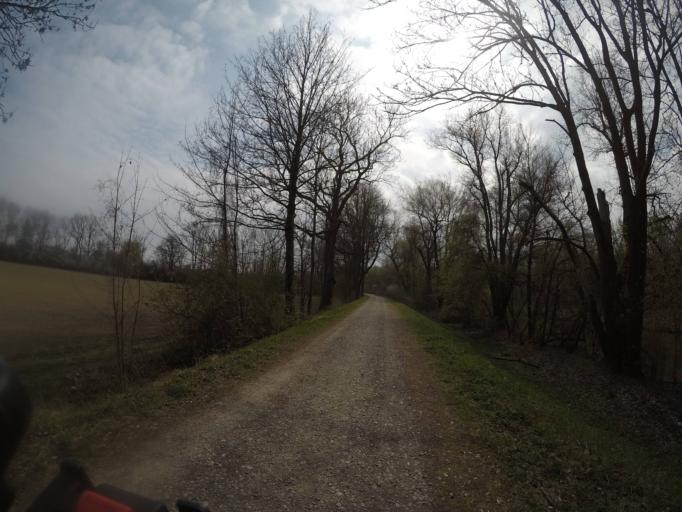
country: DE
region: Baden-Wuerttemberg
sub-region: Tuebingen Region
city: Ulm
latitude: 48.3718
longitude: 9.9759
